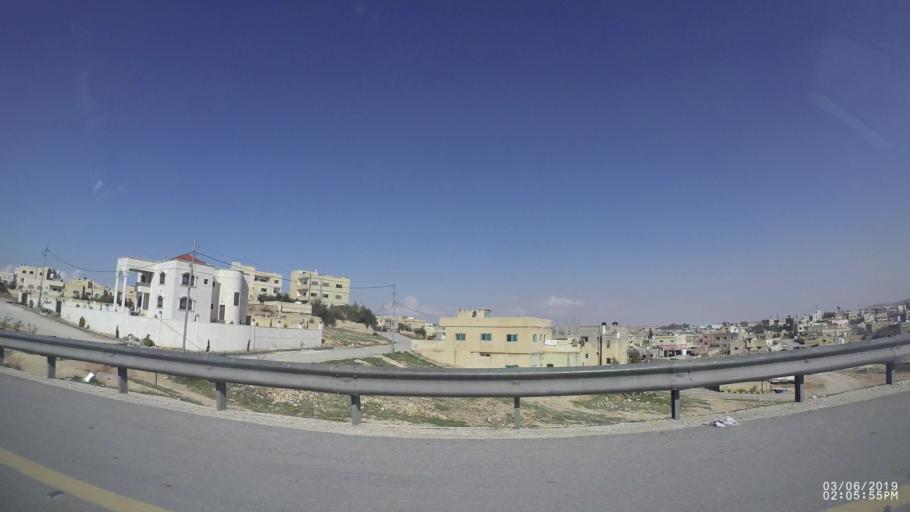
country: JO
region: Zarqa
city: Russeifa
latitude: 32.0228
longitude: 36.0762
